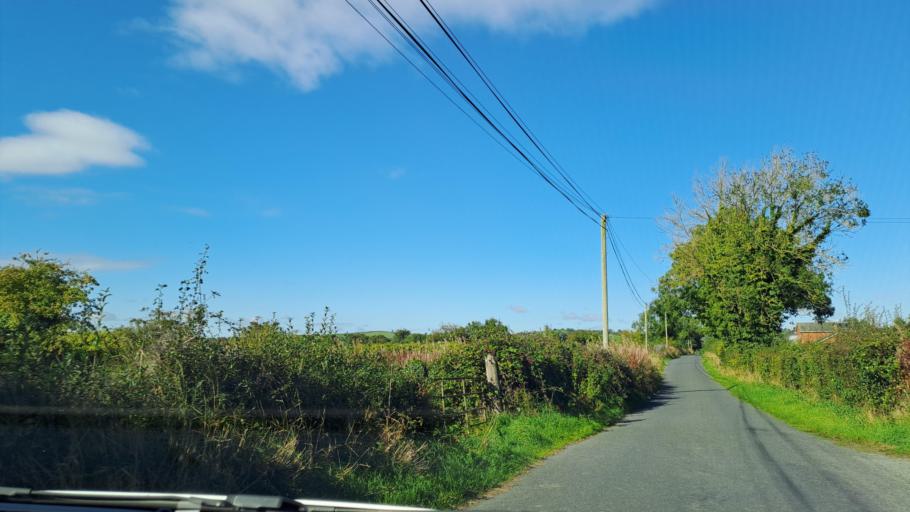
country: IE
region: Ulster
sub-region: County Monaghan
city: Carrickmacross
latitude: 53.9834
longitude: -6.7401
